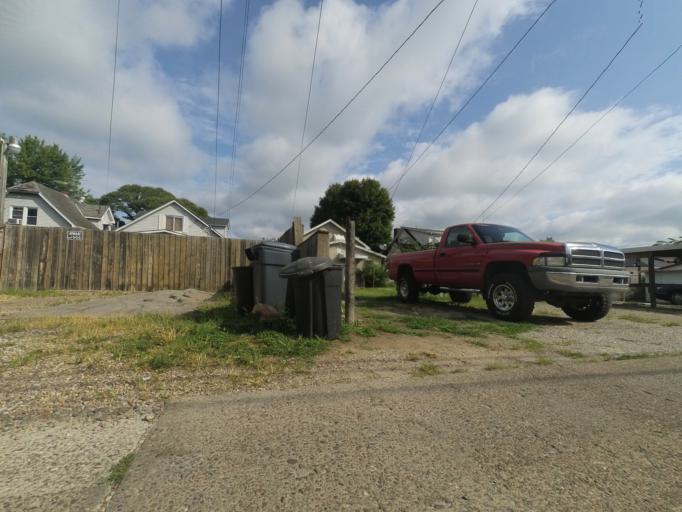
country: US
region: West Virginia
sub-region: Cabell County
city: Huntington
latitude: 38.4347
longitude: -82.4075
